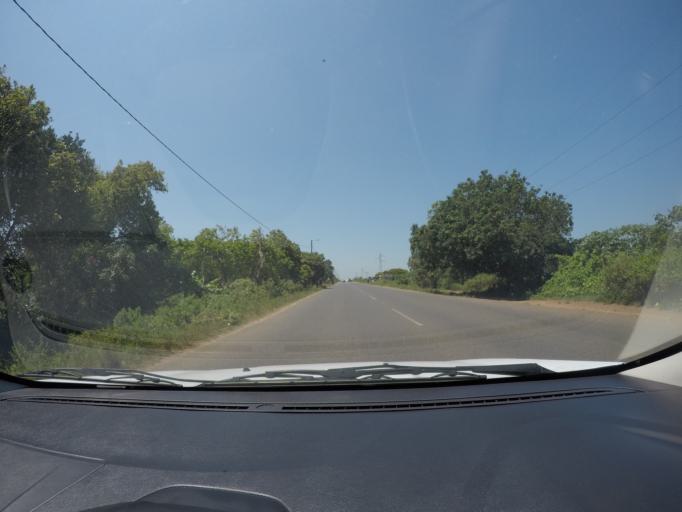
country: ZA
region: KwaZulu-Natal
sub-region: uThungulu District Municipality
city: eSikhawini
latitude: -28.8431
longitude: 31.9337
